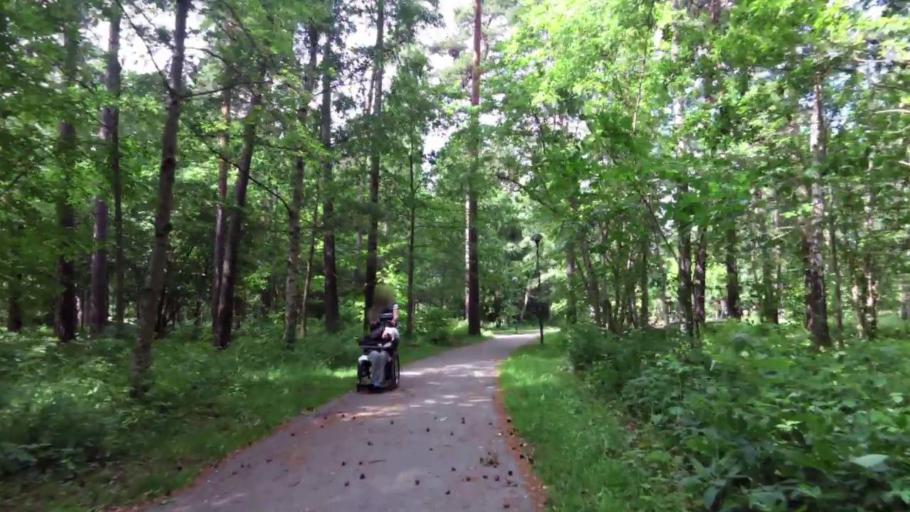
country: SE
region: OEstergoetland
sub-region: Linkopings Kommun
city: Linkoping
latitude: 58.4108
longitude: 15.6006
